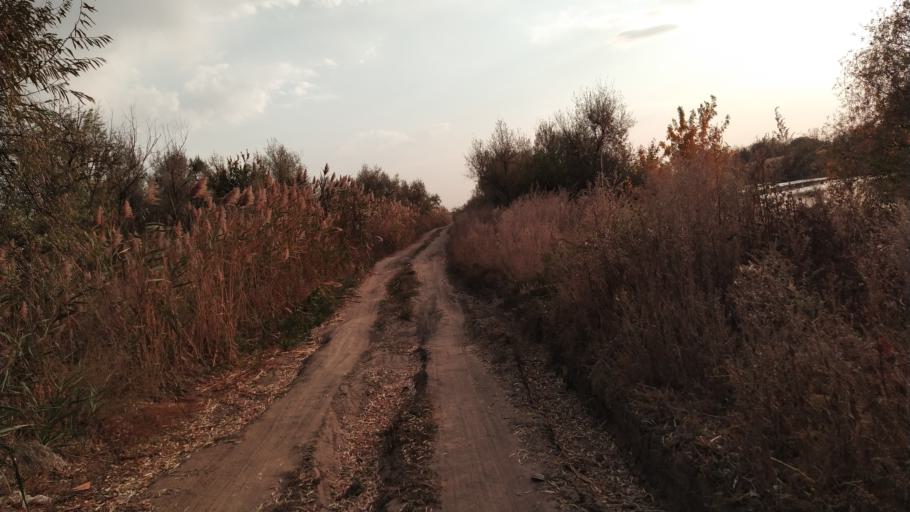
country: RU
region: Rostov
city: Kuleshovka
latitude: 47.1215
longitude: 39.6039
